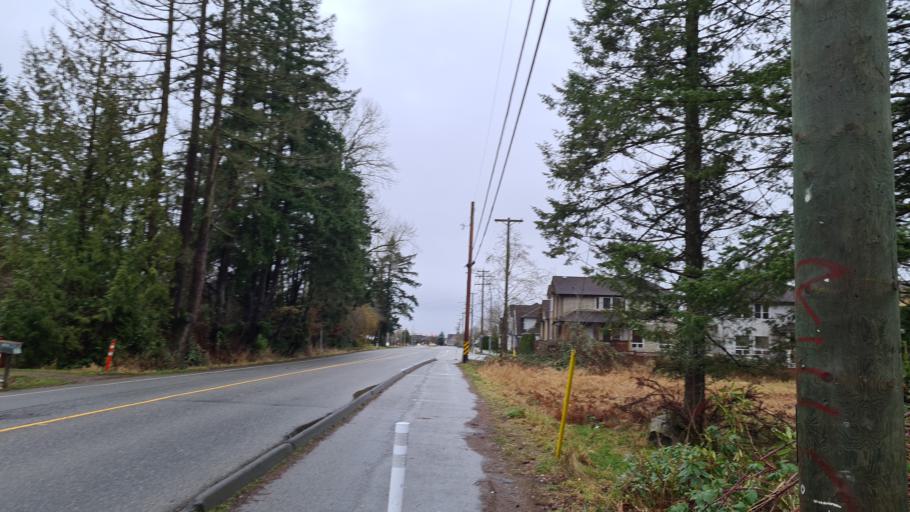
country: CA
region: British Columbia
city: Walnut Grove
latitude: 49.1376
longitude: -122.6615
